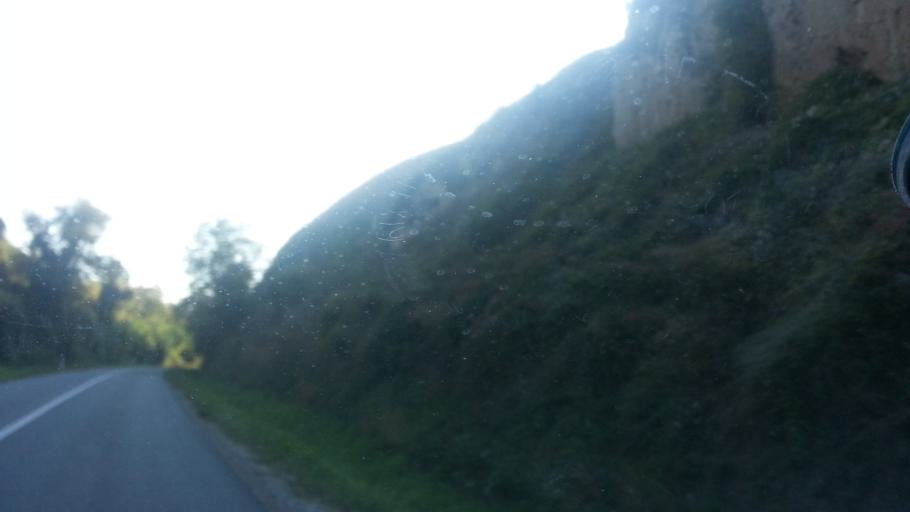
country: RS
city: Novi Slankamen
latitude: 45.1380
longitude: 20.2539
